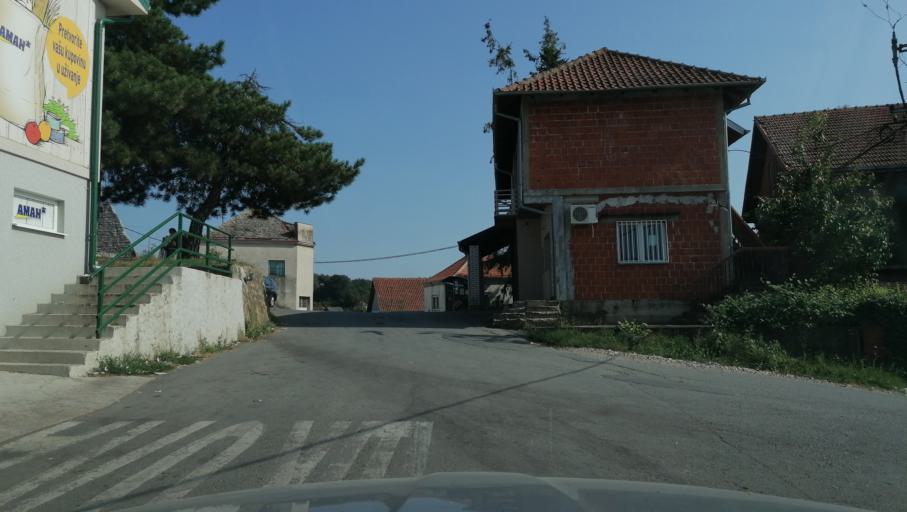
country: RS
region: Central Serbia
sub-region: Belgrade
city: Sopot
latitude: 44.5845
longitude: 20.6083
